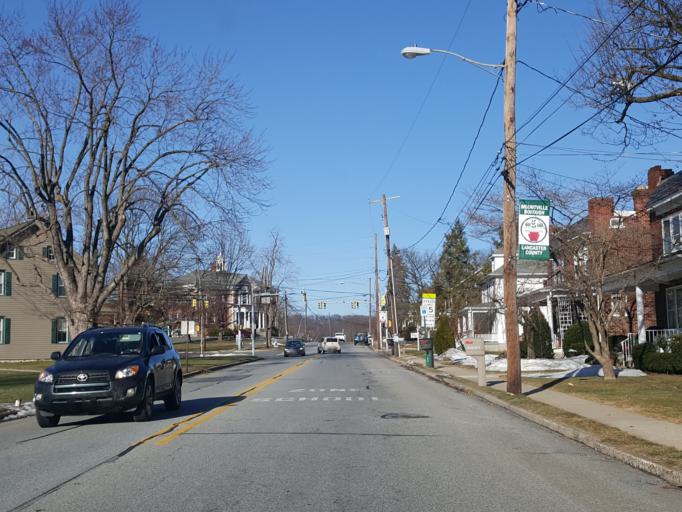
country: US
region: Pennsylvania
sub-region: Lancaster County
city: Mountville
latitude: 40.0405
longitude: -76.4271
